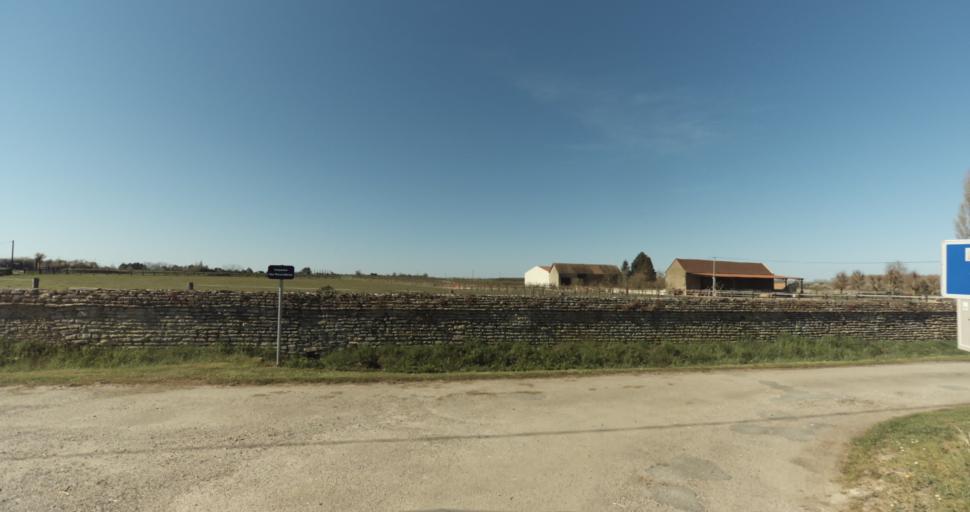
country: FR
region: Lower Normandy
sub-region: Departement du Calvados
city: Saint-Pierre-sur-Dives
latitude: 49.0522
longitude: -0.0504
